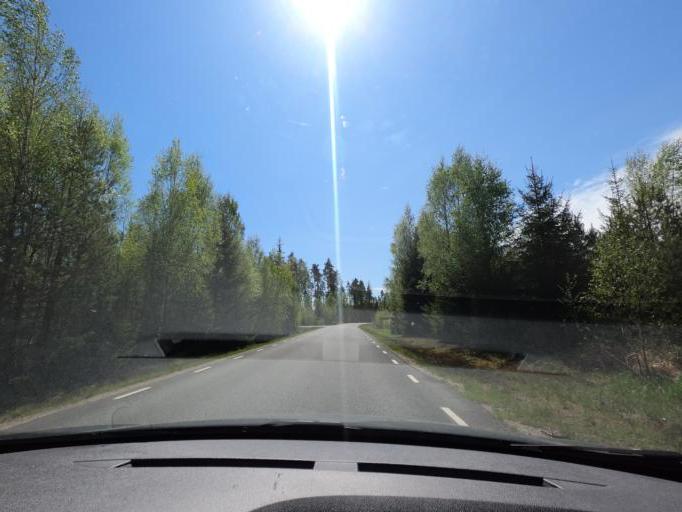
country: SE
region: Joenkoeping
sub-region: Varnamo Kommun
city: Bredaryd
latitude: 57.1572
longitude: 13.7359
